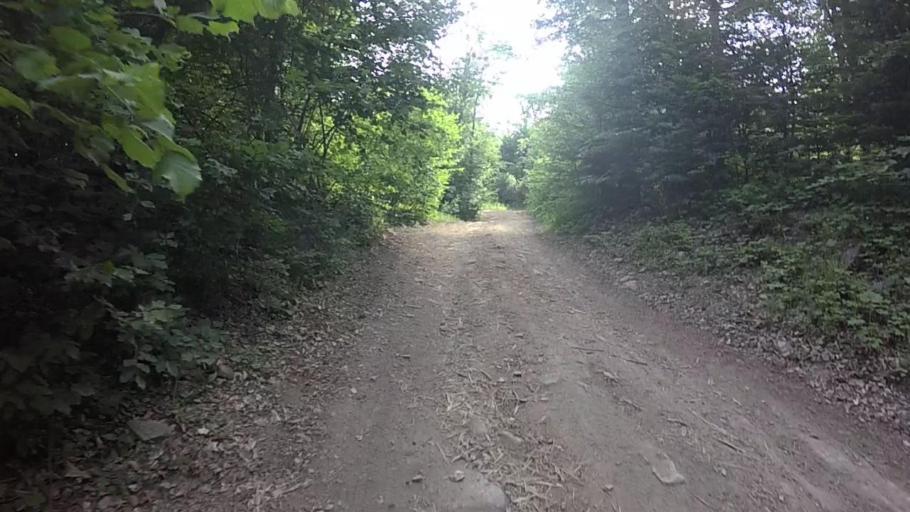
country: FR
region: Provence-Alpes-Cote d'Azur
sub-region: Departement des Alpes-de-Haute-Provence
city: Seyne-les-Alpes
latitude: 44.4054
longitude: 6.3524
